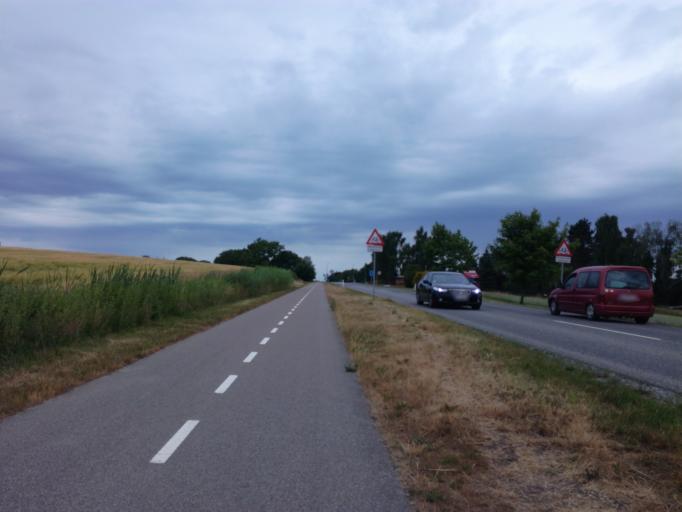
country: DK
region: South Denmark
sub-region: Vejle Kommune
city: Borkop
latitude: 55.6619
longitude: 9.6298
